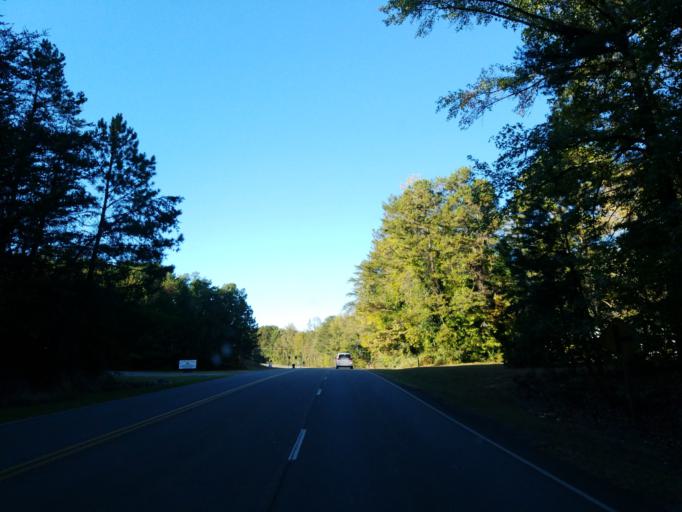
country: US
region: Georgia
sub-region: Pickens County
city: Nelson
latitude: 34.3864
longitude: -84.3755
